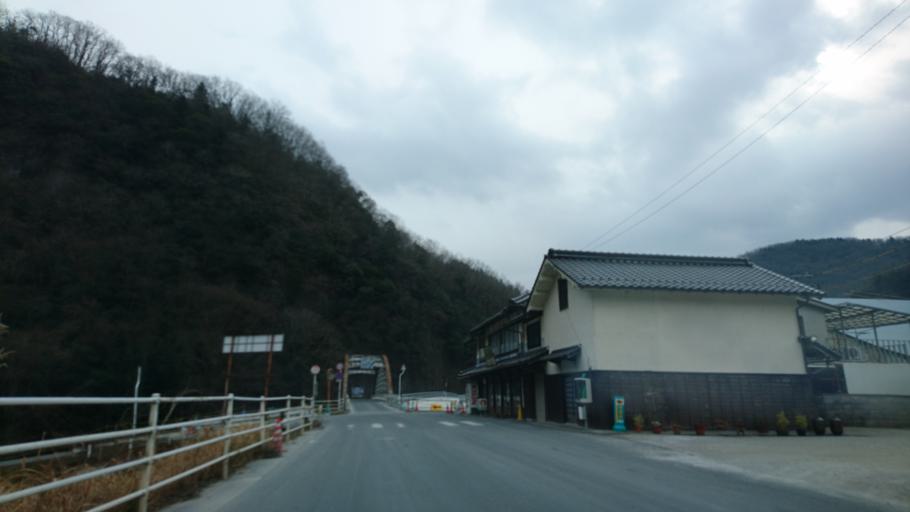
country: JP
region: Okayama
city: Niimi
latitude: 34.9264
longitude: 133.5211
